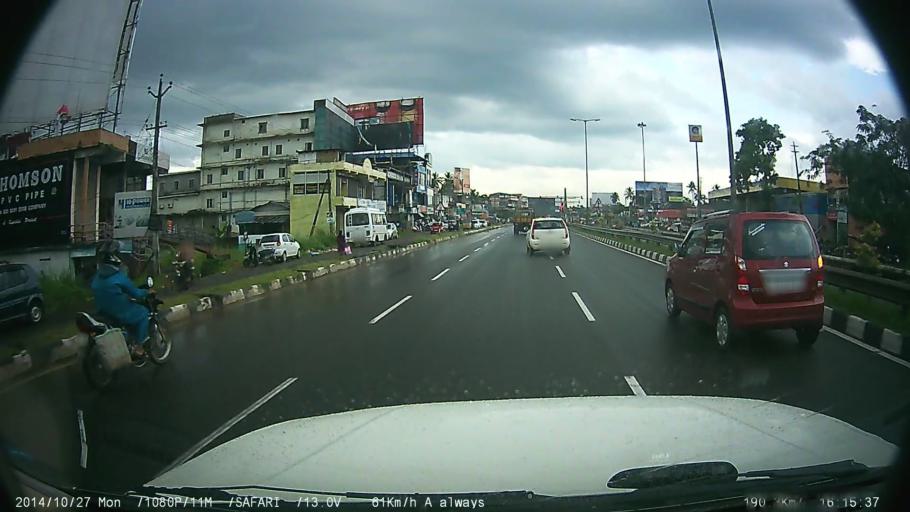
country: IN
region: Kerala
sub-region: Thrissur District
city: Trichur
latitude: 10.4308
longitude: 76.2662
